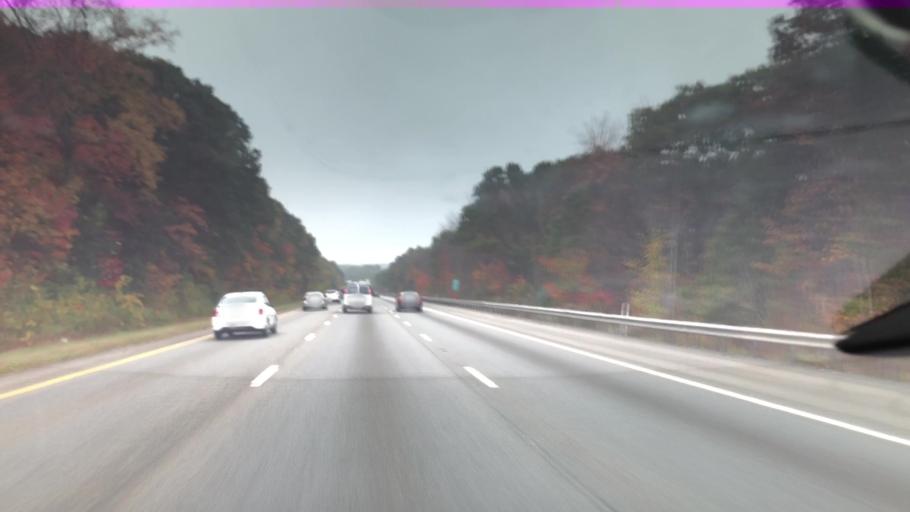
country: US
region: Massachusetts
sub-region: Worcester County
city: Harvard
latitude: 42.5037
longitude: -71.5290
